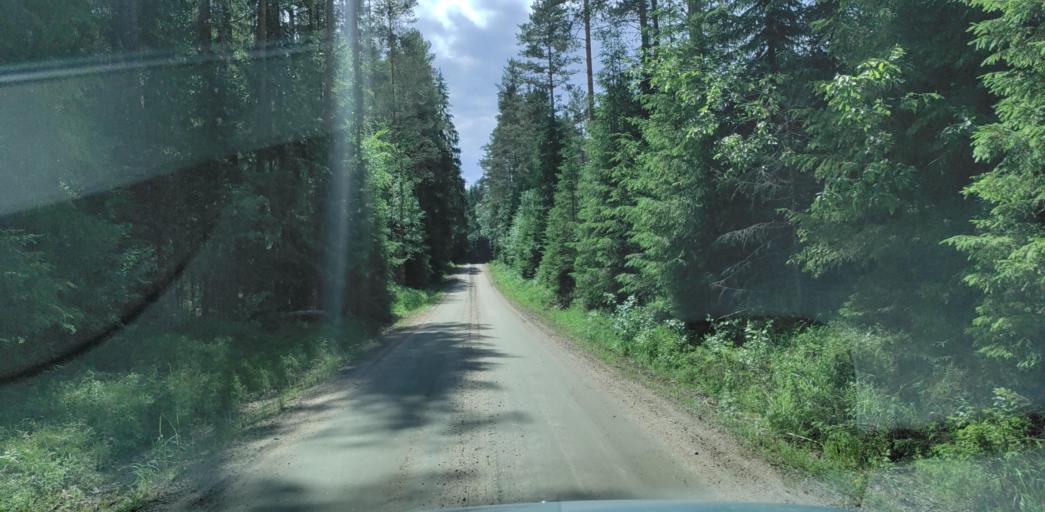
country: SE
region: Vaermland
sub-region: Sunne Kommun
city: Sunne
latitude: 60.0436
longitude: 13.2546
